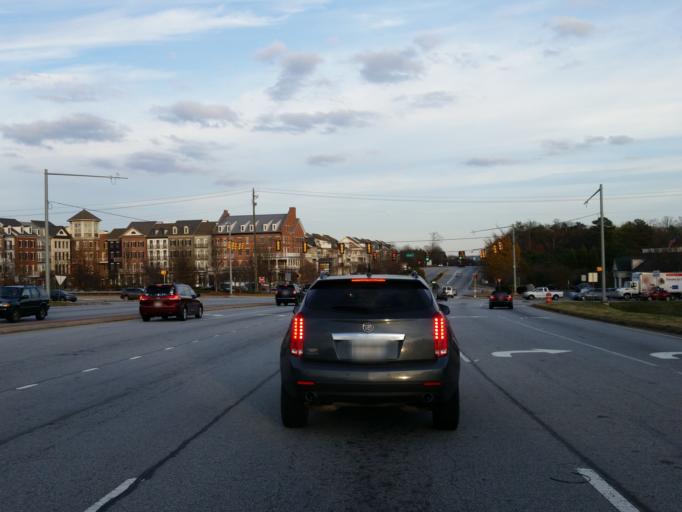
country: US
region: Georgia
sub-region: Cobb County
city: Vinings
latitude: 33.8486
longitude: -84.4942
